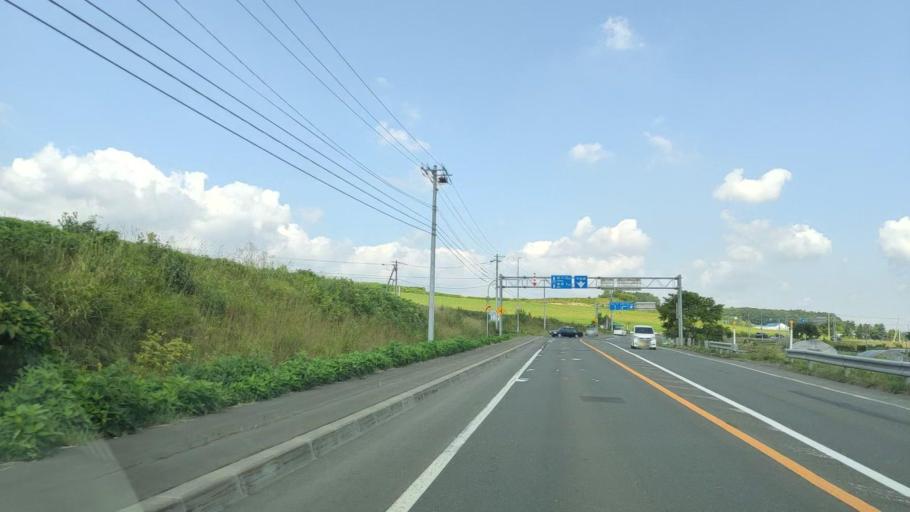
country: JP
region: Hokkaido
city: Shimo-furano
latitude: 43.5321
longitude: 142.4420
